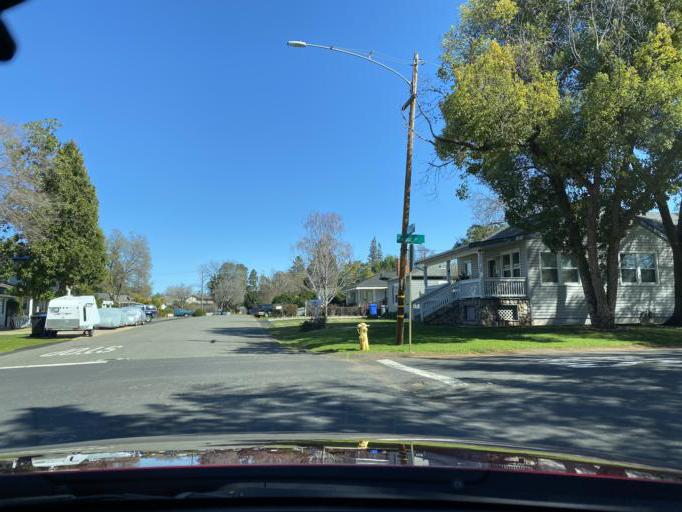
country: US
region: California
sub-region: Sacramento County
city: Folsom
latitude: 38.6777
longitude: -121.1724
